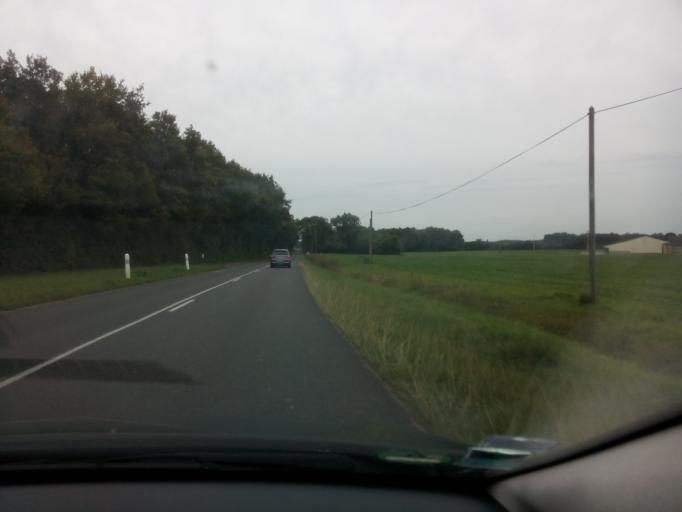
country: FR
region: Pays de la Loire
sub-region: Departement de Maine-et-Loire
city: Seiches-sur-le-Loir
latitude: 47.5537
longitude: -0.3322
